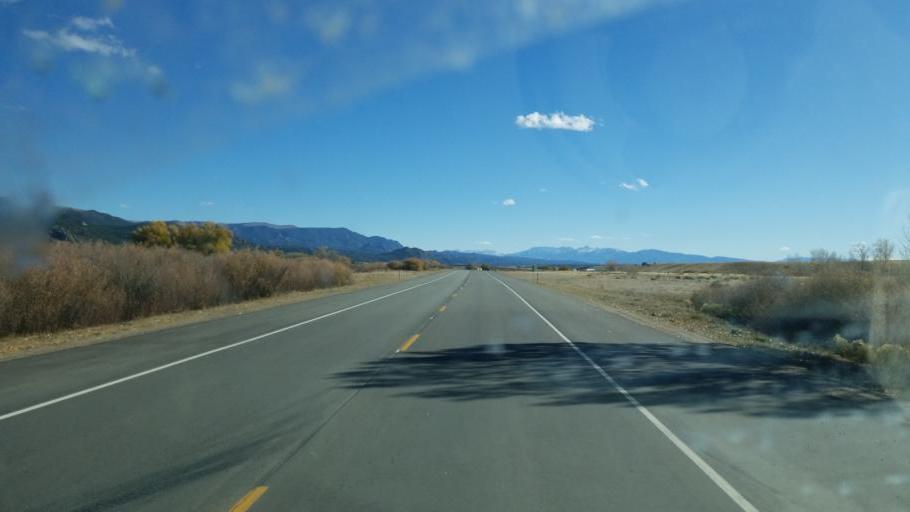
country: US
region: Colorado
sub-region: Chaffee County
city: Buena Vista
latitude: 38.8227
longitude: -106.1222
